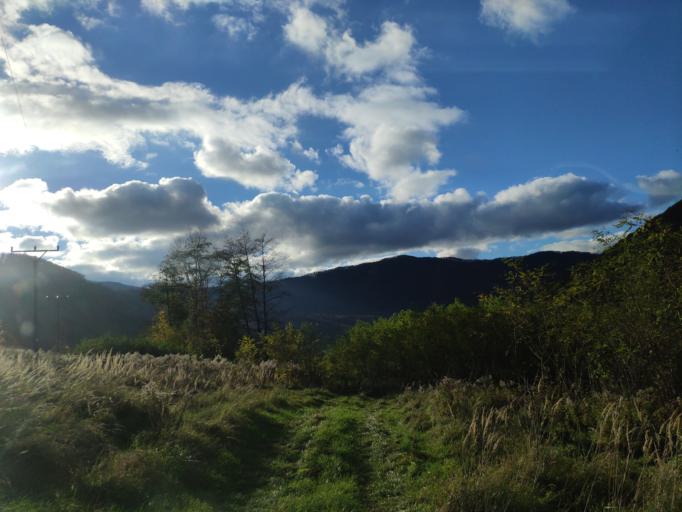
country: SK
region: Presovsky
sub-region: Okres Presov
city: Presov
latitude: 48.8550
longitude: 21.1870
